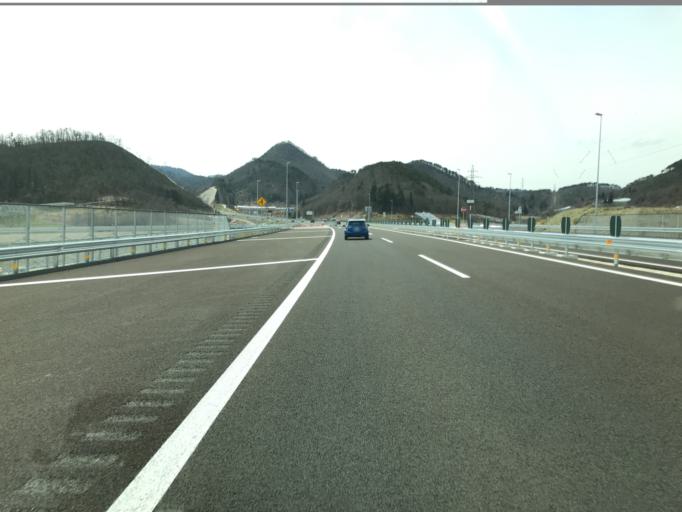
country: JP
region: Yamagata
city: Kaminoyama
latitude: 38.1271
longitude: 140.2571
